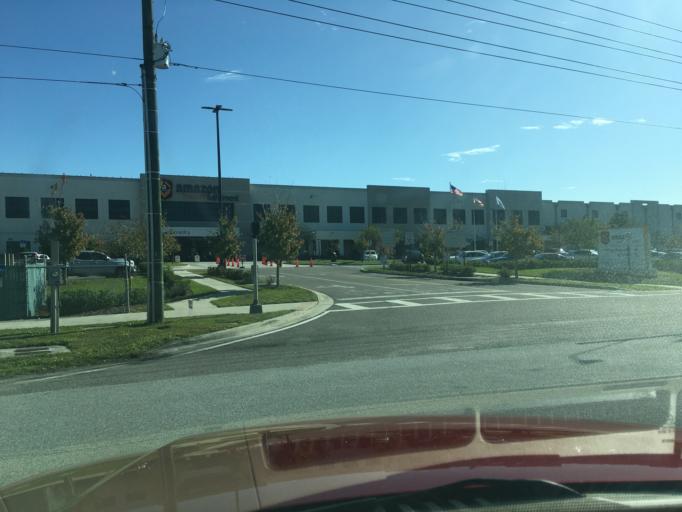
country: US
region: Florida
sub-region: Polk County
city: Winston
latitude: 28.0202
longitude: -82.0556
